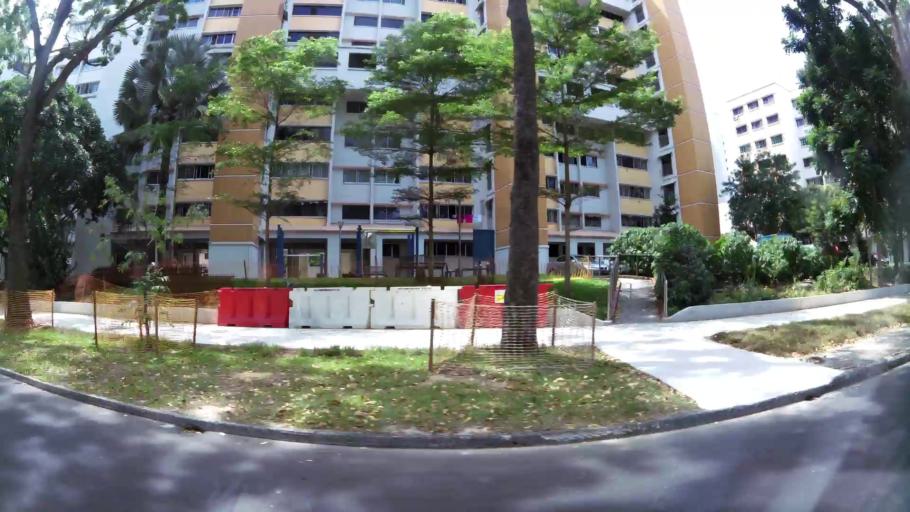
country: MY
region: Johor
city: Johor Bahru
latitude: 1.3527
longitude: 103.7246
